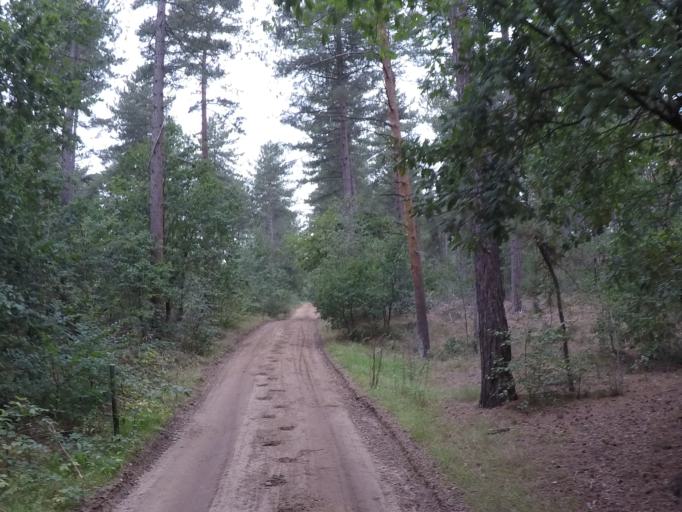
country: BE
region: Flanders
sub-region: Provincie Antwerpen
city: Kasterlee
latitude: 51.2395
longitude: 4.9512
